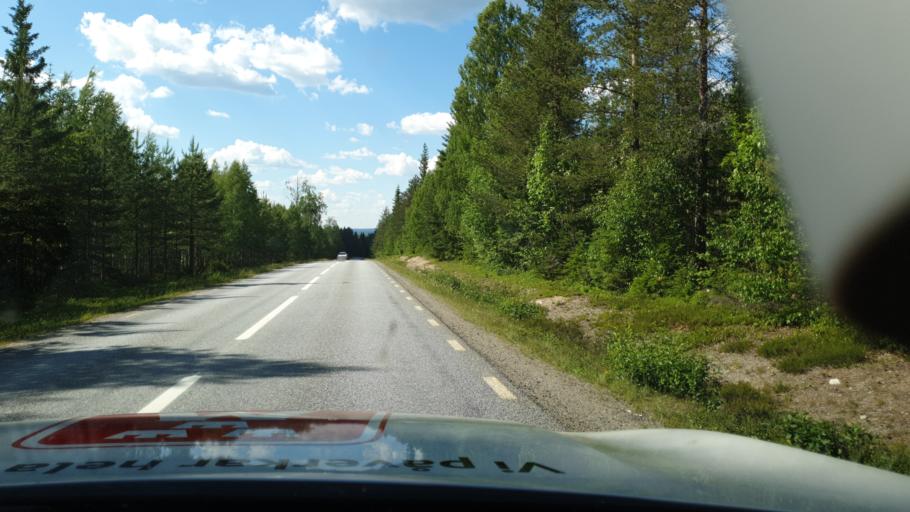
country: SE
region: Vaesterbotten
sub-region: Skelleftea Kommun
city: Burtraesk
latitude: 64.5054
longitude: 20.5065
